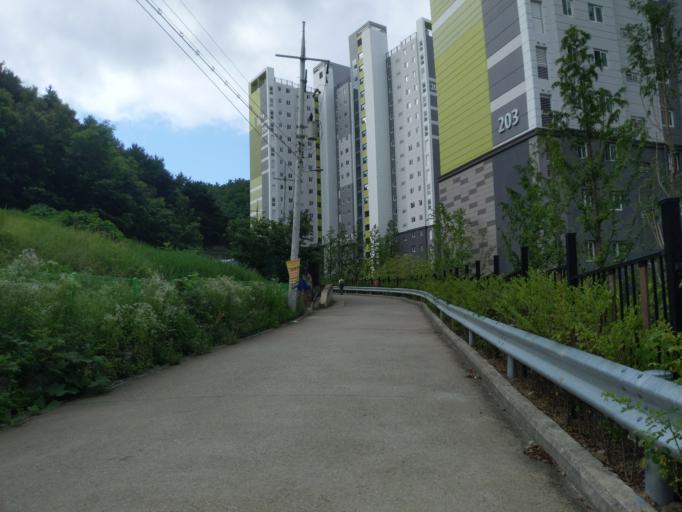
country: KR
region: Daegu
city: Hwawon
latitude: 35.7991
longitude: 128.5324
